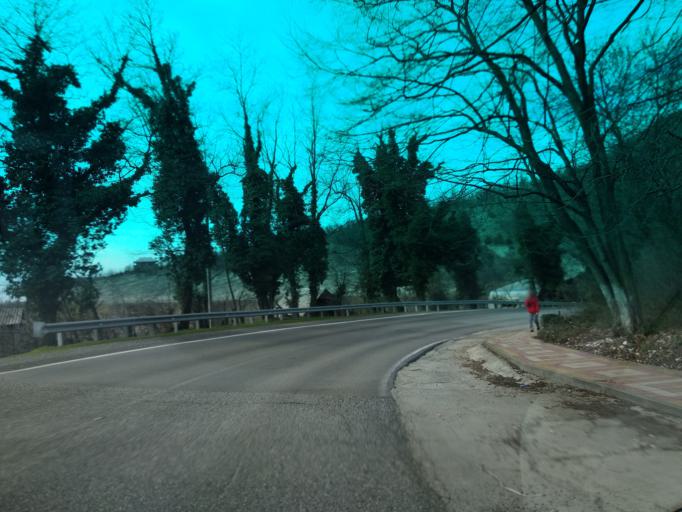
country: RU
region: Krasnodarskiy
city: Tuapse
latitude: 44.0857
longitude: 39.1287
